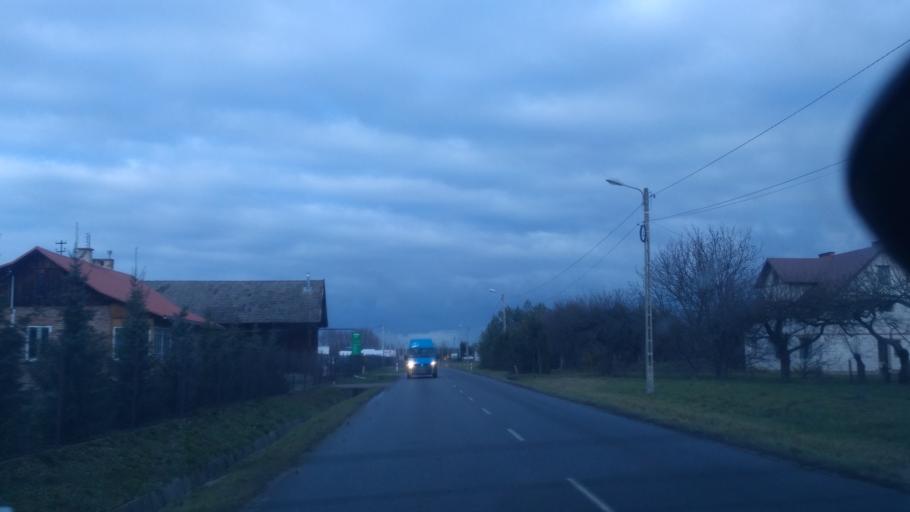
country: PL
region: Subcarpathian Voivodeship
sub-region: Powiat lancucki
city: Czarna
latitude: 50.0972
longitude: 22.1859
